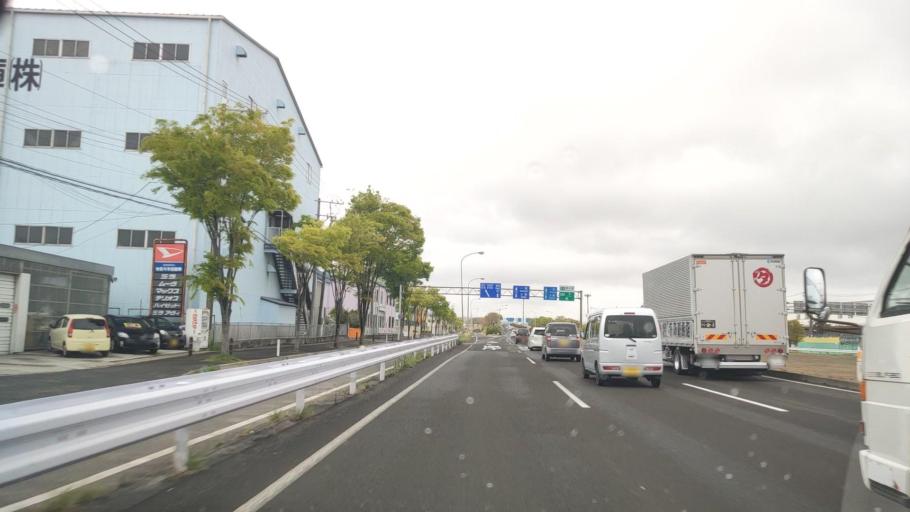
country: JP
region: Miyagi
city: Sendai-shi
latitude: 38.2627
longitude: 140.9378
